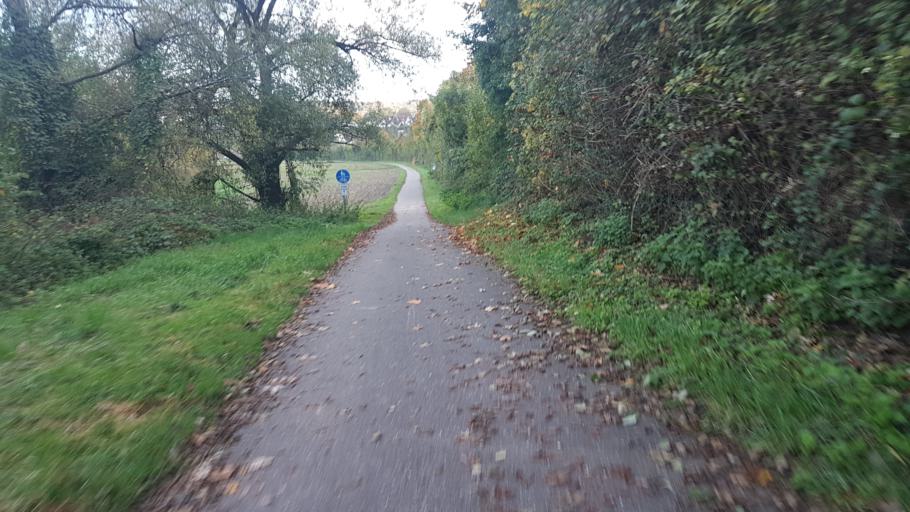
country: DE
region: Baden-Wuerttemberg
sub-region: Karlsruhe Region
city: Obrigheim
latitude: 49.3298
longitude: 9.0982
